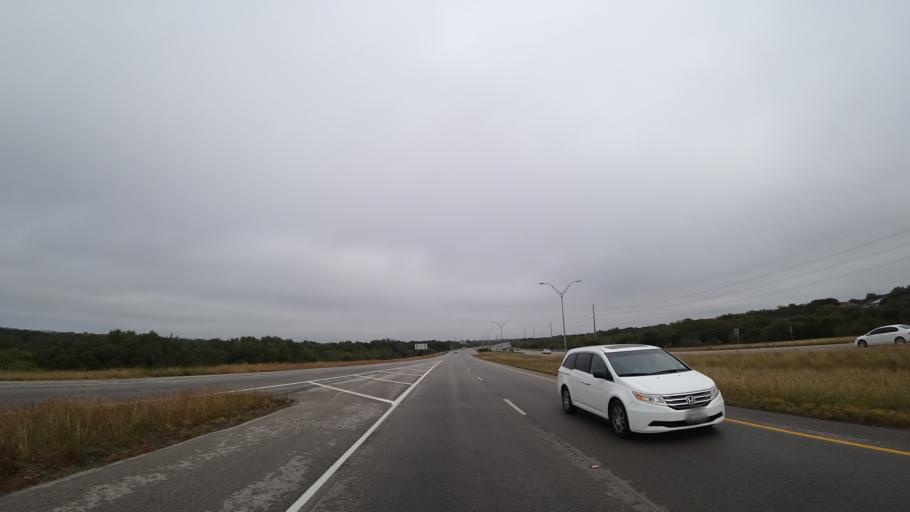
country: US
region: Texas
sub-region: Travis County
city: Shady Hollow
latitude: 30.2107
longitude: -97.8590
